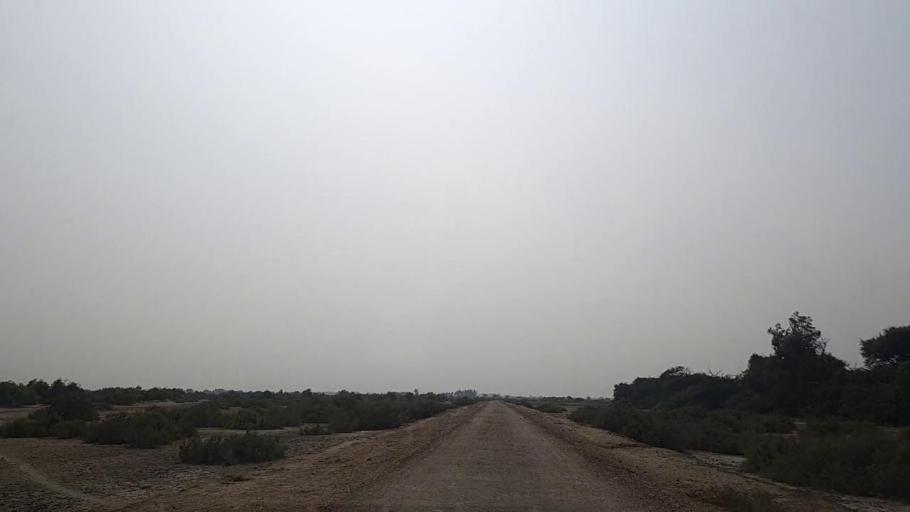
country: PK
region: Sindh
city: Mirpur Sakro
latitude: 24.6457
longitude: 67.7676
